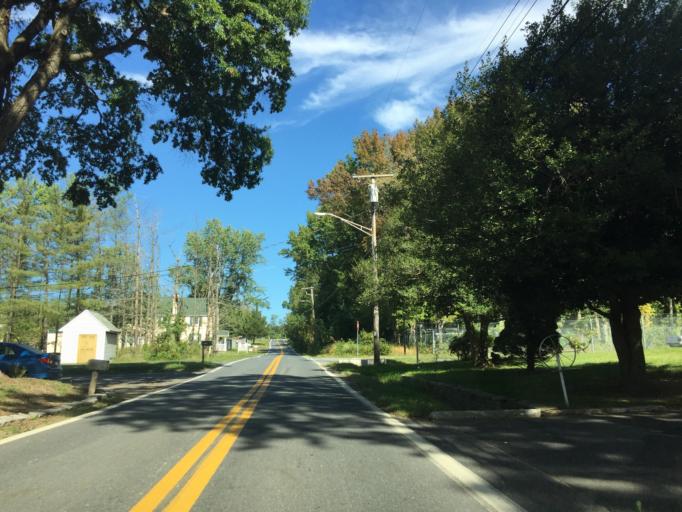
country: US
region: Maryland
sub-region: Baltimore County
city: White Marsh
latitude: 39.3955
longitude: -76.4130
